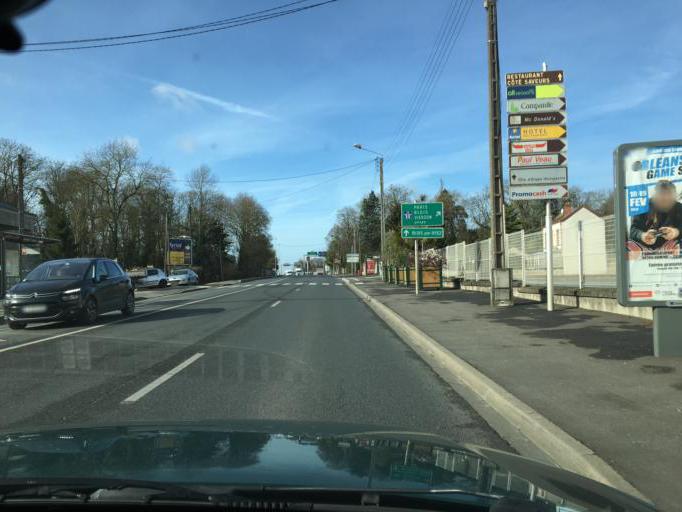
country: FR
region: Centre
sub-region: Departement du Loiret
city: Saint-Jean-de-la-Ruelle
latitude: 47.8957
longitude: 1.8582
